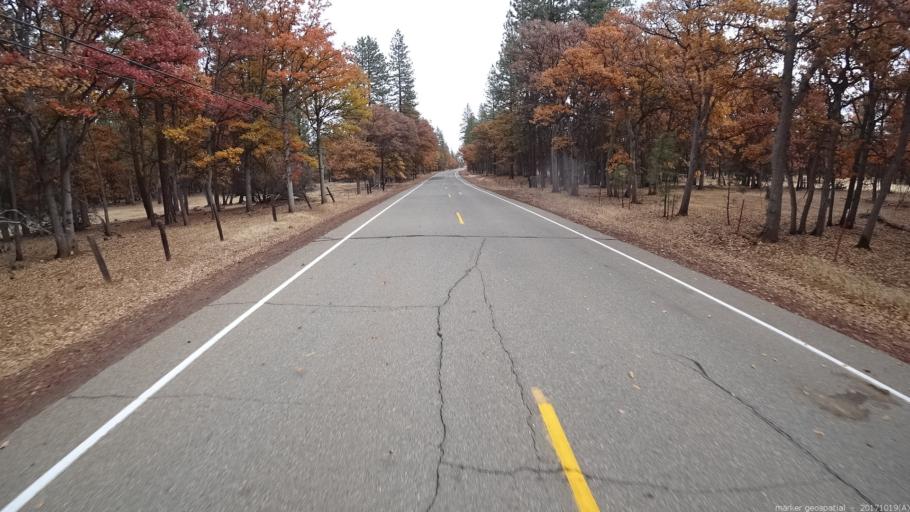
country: US
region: California
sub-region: Shasta County
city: Burney
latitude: 41.0945
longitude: -121.5312
